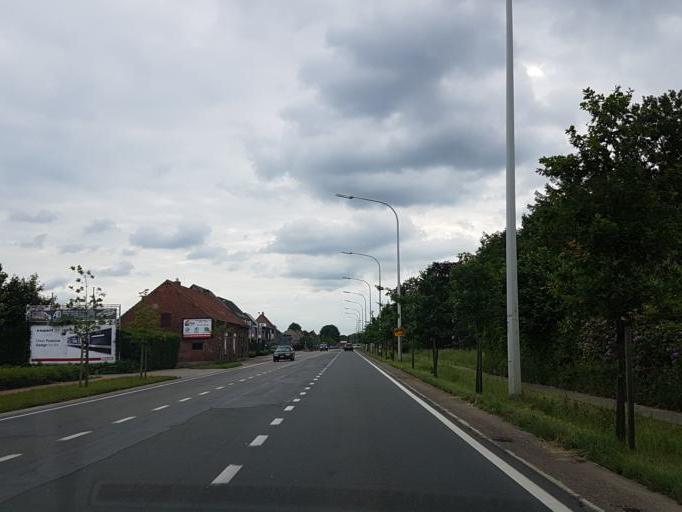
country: BE
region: Flanders
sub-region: Provincie Antwerpen
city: Oostmalle
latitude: 51.2983
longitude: 4.7072
